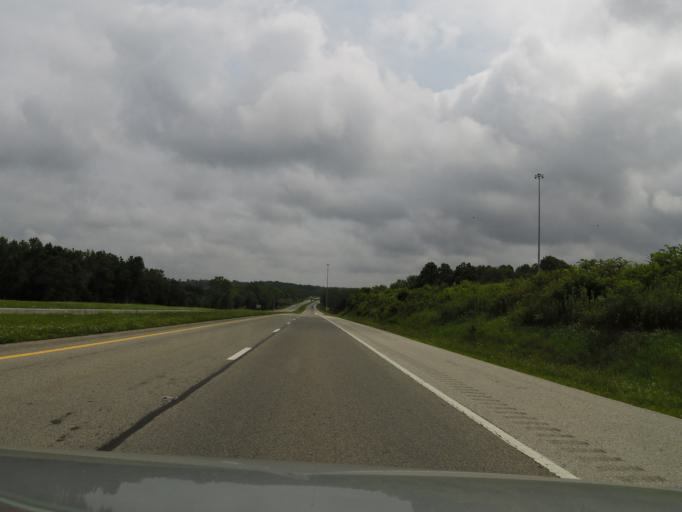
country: US
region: Kentucky
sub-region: Ohio County
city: Oak Grove
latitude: 37.3853
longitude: -86.8074
